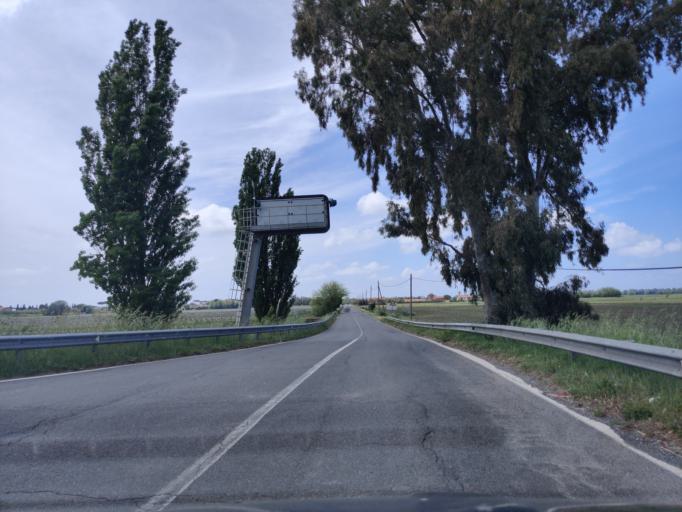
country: IT
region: Latium
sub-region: Citta metropolitana di Roma Capitale
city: Maccarese
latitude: 41.8851
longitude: 12.2228
